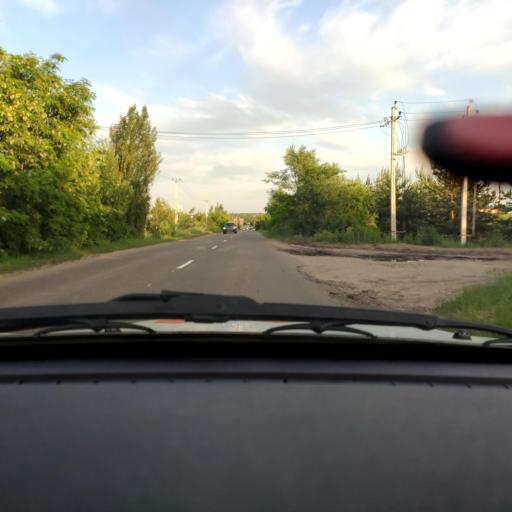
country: RU
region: Voronezj
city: Podgornoye
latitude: 51.8338
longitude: 39.2034
